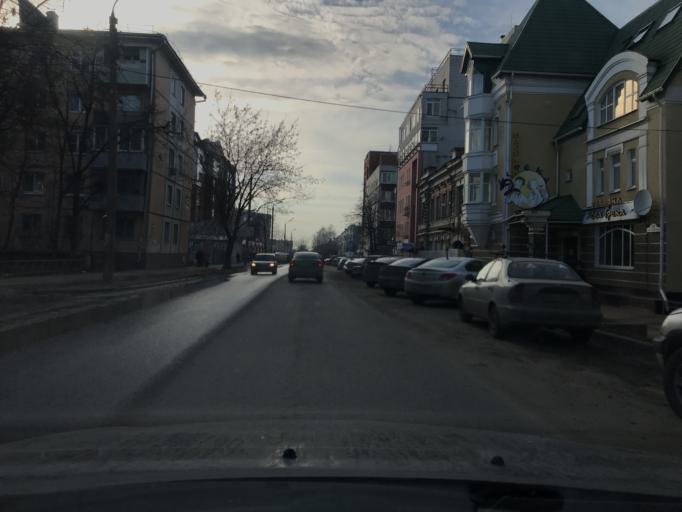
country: RU
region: Kaluga
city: Kaluga
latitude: 54.5181
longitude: 36.2447
